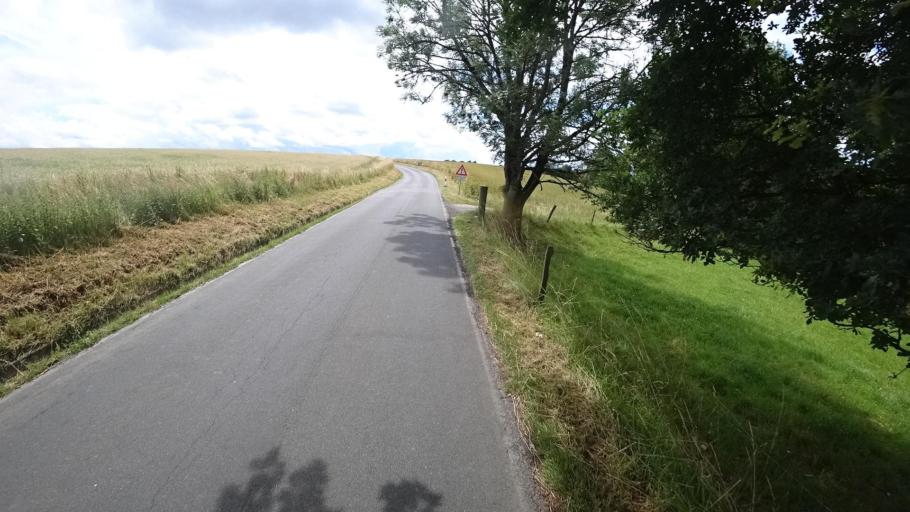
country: DE
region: Rheinland-Pfalz
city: Fiersbach
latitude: 50.6943
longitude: 7.4998
